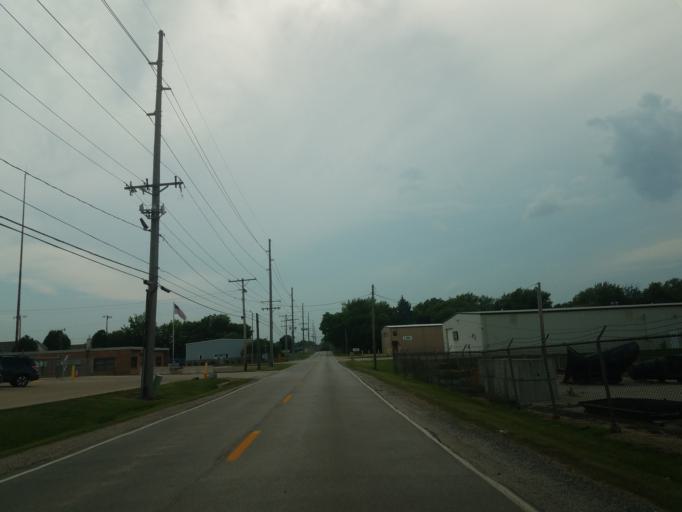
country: US
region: Illinois
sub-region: McLean County
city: Bloomington
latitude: 40.4634
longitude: -88.9872
